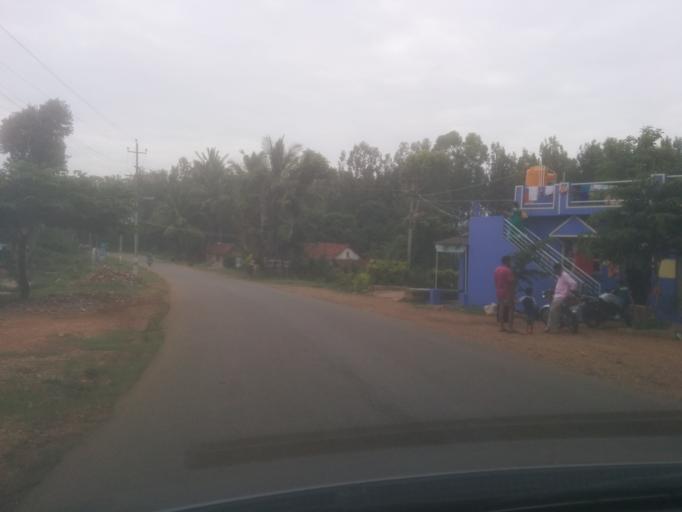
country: IN
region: Karnataka
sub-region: Chikmagalur
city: Chikmagalur
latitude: 13.3539
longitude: 75.7598
